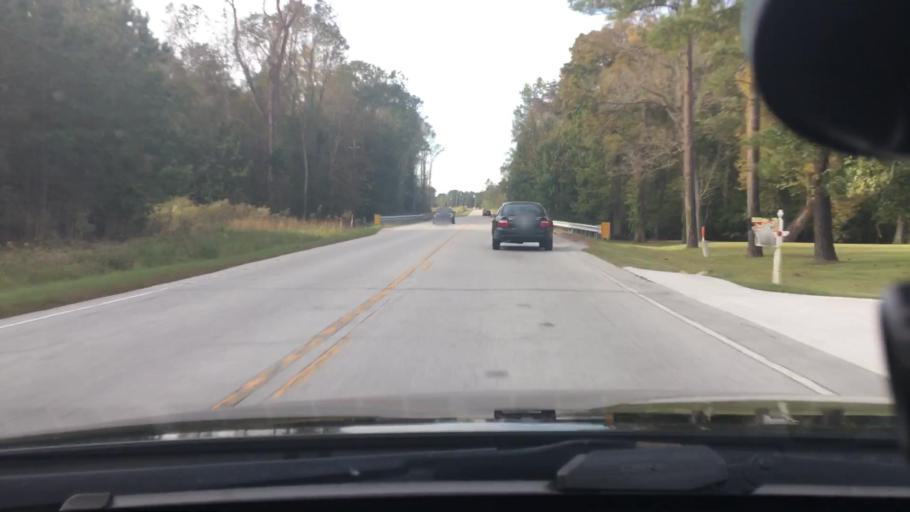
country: US
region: North Carolina
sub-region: Craven County
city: Vanceboro
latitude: 35.3362
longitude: -77.1736
